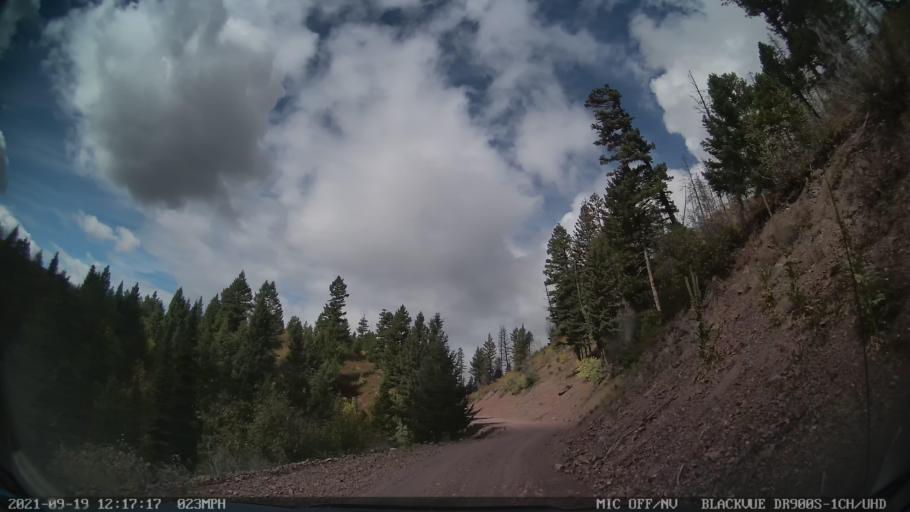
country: US
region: Montana
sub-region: Missoula County
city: Seeley Lake
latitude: 47.1716
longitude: -113.3571
